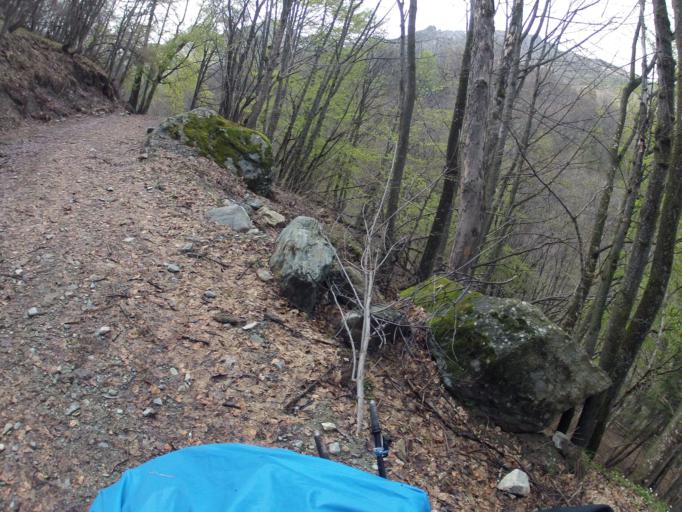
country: IT
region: Piedmont
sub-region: Provincia di Cuneo
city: Crissolo
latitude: 44.7012
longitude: 7.1459
